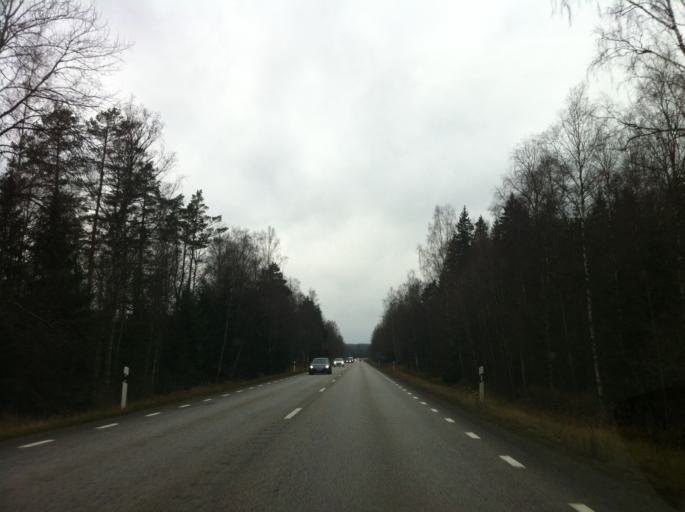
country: SE
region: Joenkoeping
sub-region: Vetlanda Kommun
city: Vetlanda
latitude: 57.4271
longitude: 15.0548
